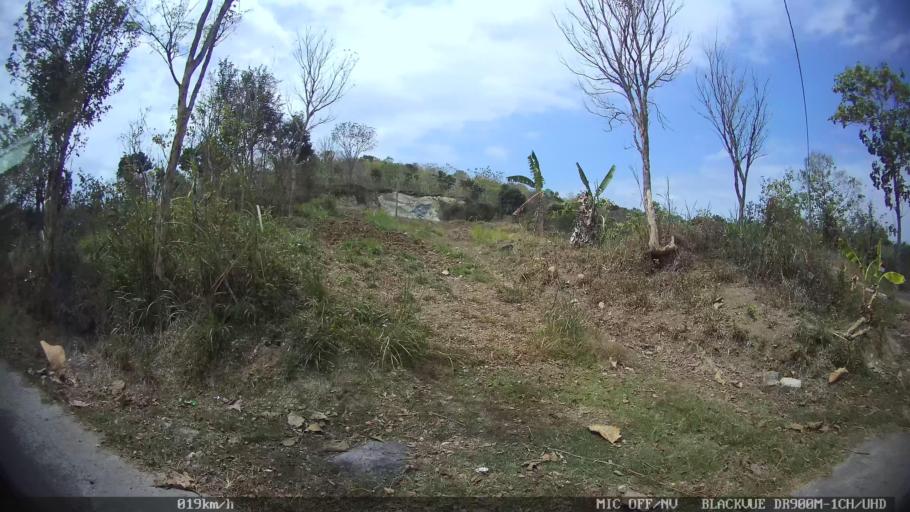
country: ID
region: Central Java
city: Candi Prambanan
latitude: -7.8081
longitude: 110.5215
